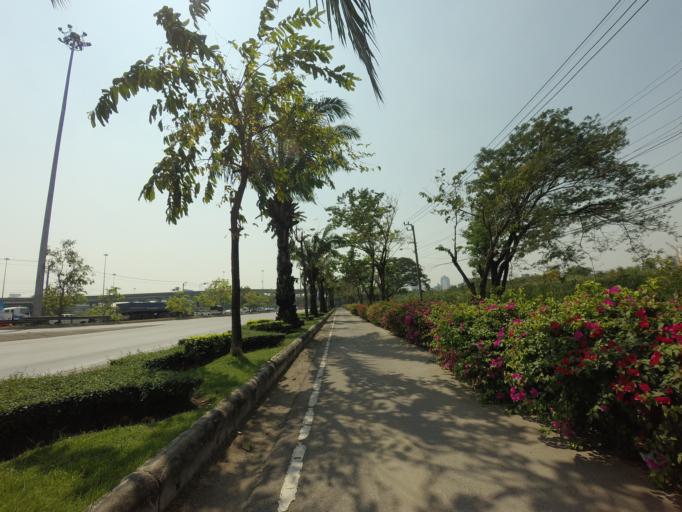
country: TH
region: Bangkok
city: Watthana
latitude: 13.7545
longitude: 100.5942
